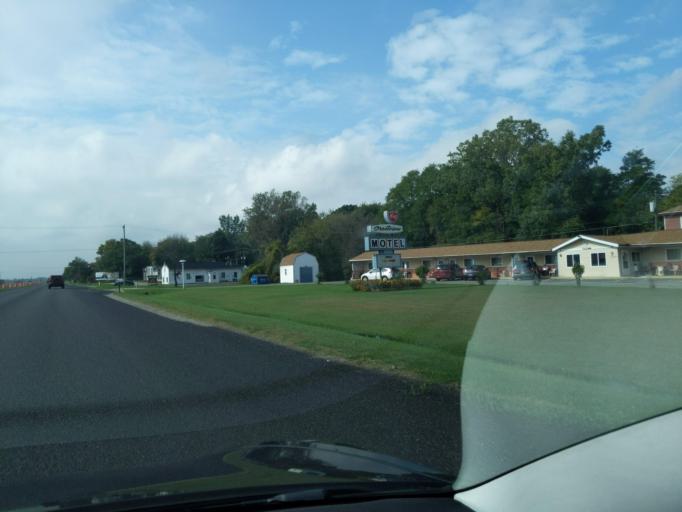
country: US
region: Michigan
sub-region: Eaton County
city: Charlotte
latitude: 42.5871
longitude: -84.8002
